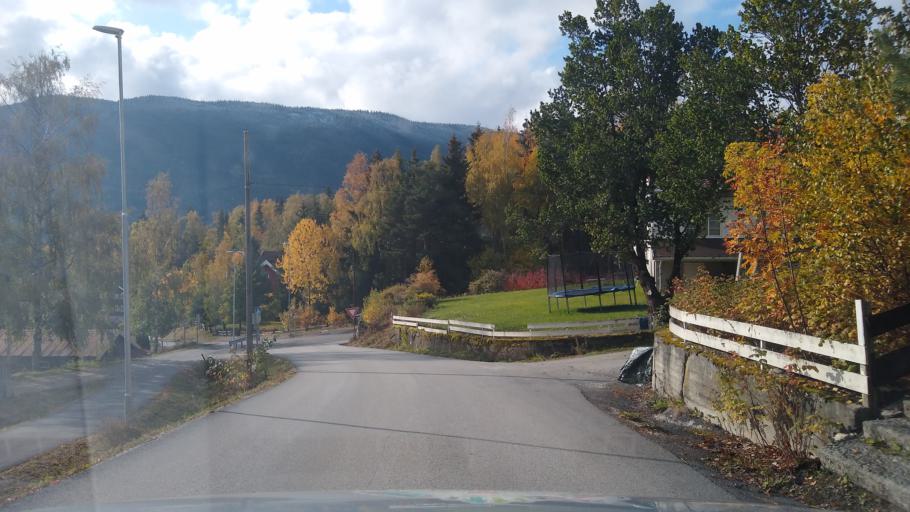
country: NO
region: Oppland
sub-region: Ringebu
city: Ringebu
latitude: 61.5339
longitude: 10.1386
